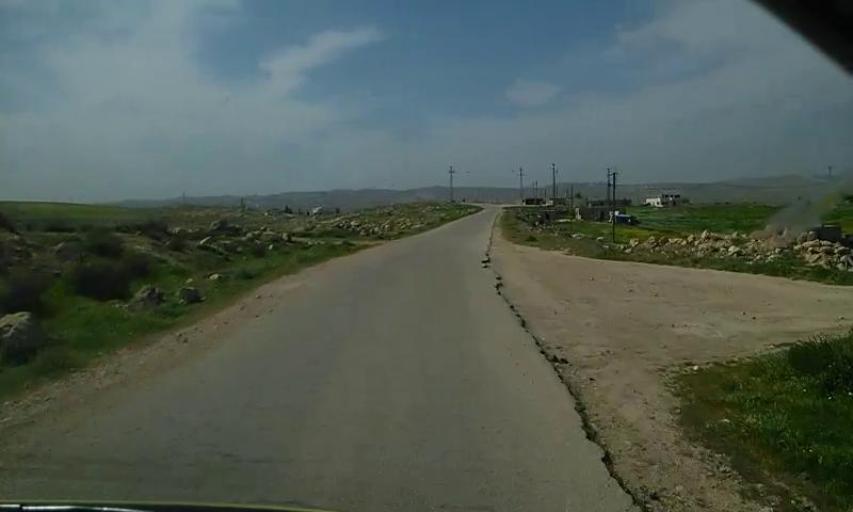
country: PS
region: West Bank
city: Khallat al Mayyah
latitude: 31.4411
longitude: 35.1998
